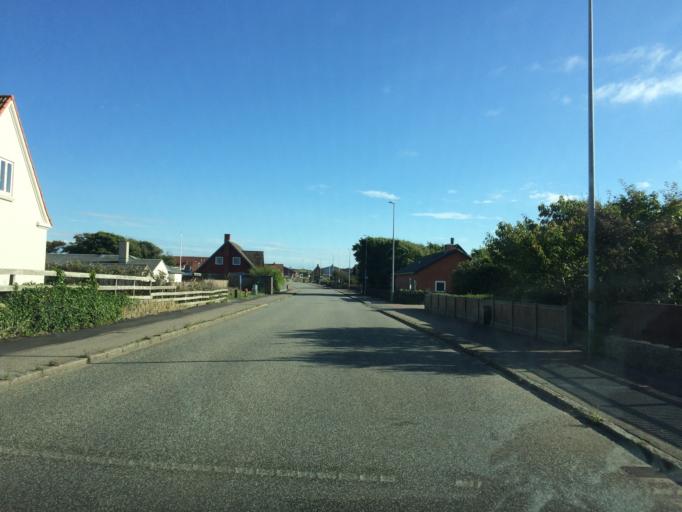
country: DK
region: Central Jutland
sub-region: Ringkobing-Skjern Kommune
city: Hvide Sande
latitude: 56.0111
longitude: 8.1273
